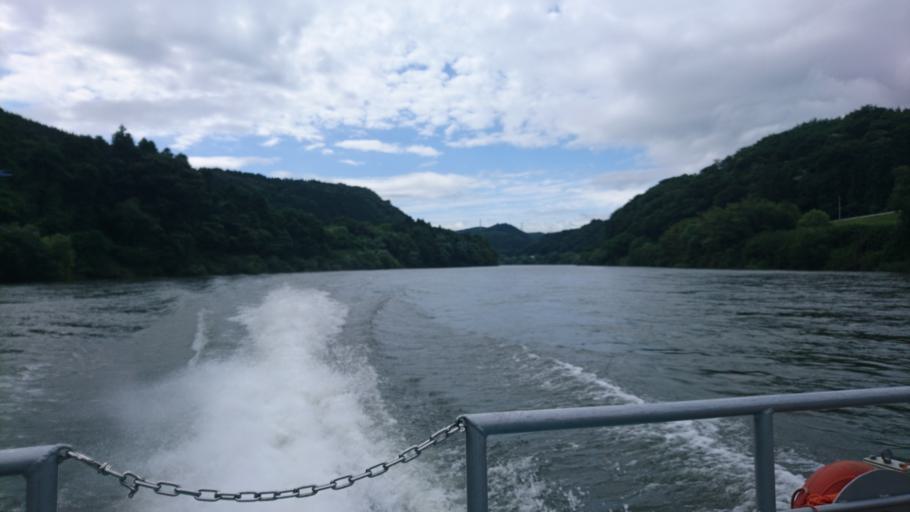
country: JP
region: Iwate
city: Ichinoseki
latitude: 38.9042
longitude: 141.2494
